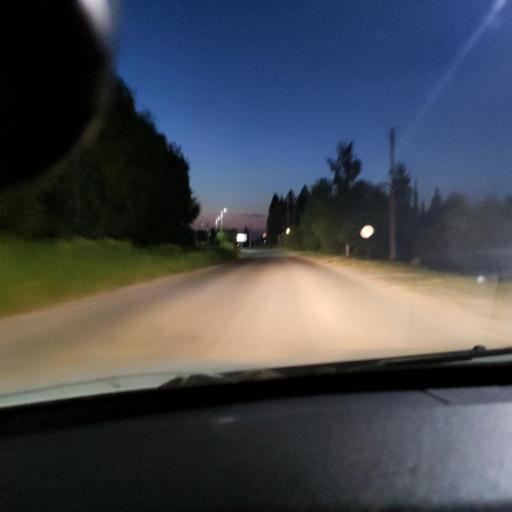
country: RU
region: Perm
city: Polazna
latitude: 58.2812
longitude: 56.4091
